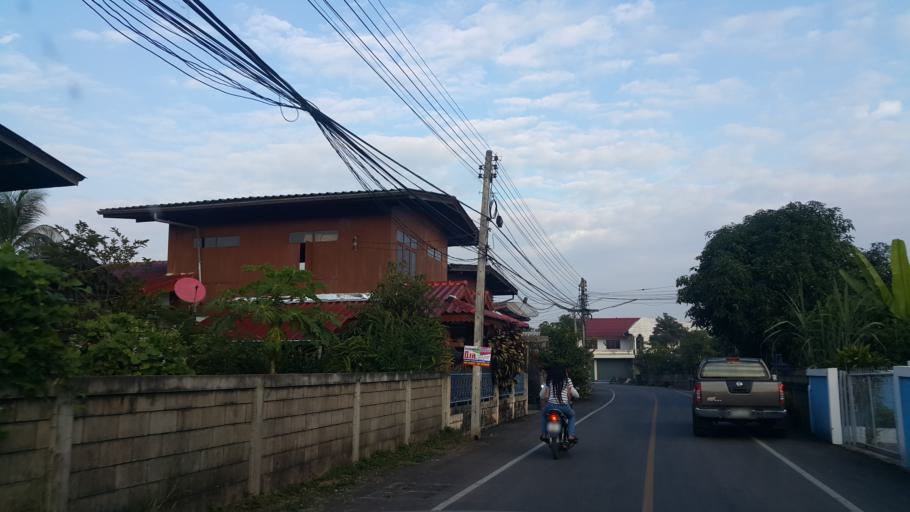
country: TH
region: Lampang
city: Sop Prap
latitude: 17.8901
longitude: 99.3335
